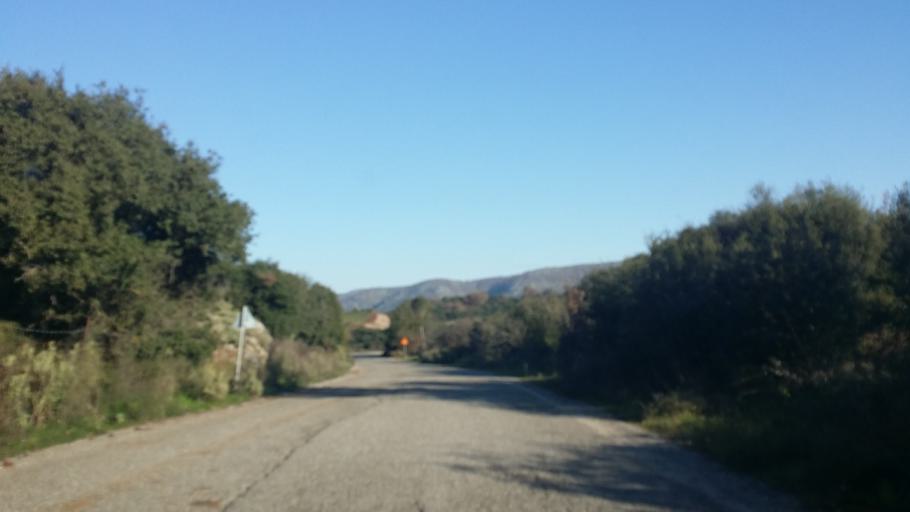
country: GR
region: West Greece
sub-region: Nomos Aitolias kai Akarnanias
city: Katouna
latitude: 38.7691
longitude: 21.1337
